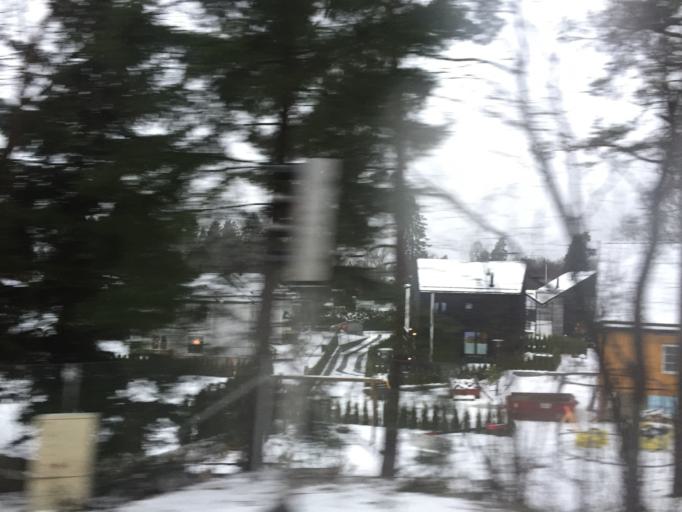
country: NO
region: Oslo
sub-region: Oslo
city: Sjolyststranda
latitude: 59.9580
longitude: 10.6963
